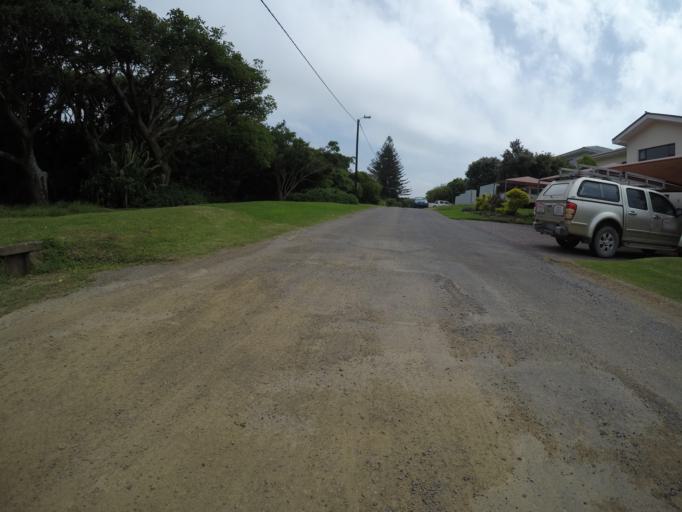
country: ZA
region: Eastern Cape
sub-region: Buffalo City Metropolitan Municipality
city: East London
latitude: -32.9397
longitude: 28.0274
